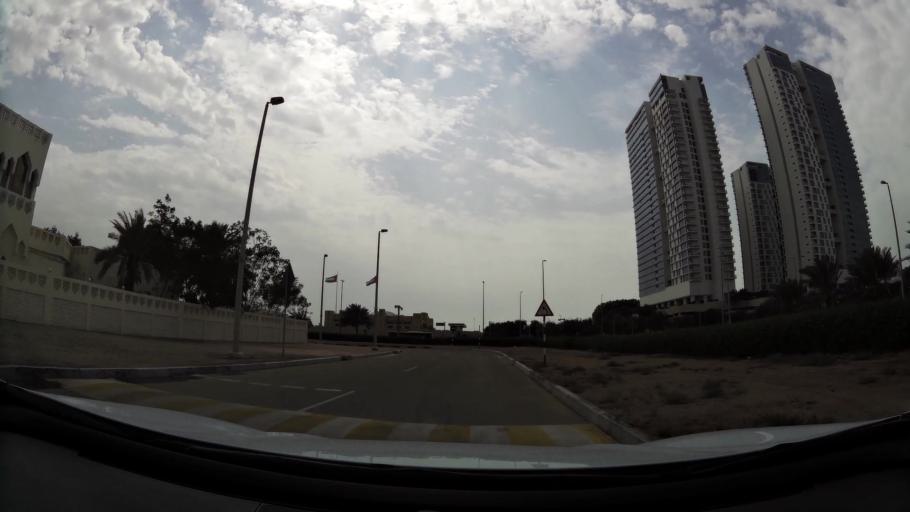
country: AE
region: Abu Dhabi
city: Abu Dhabi
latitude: 24.4153
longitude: 54.4650
